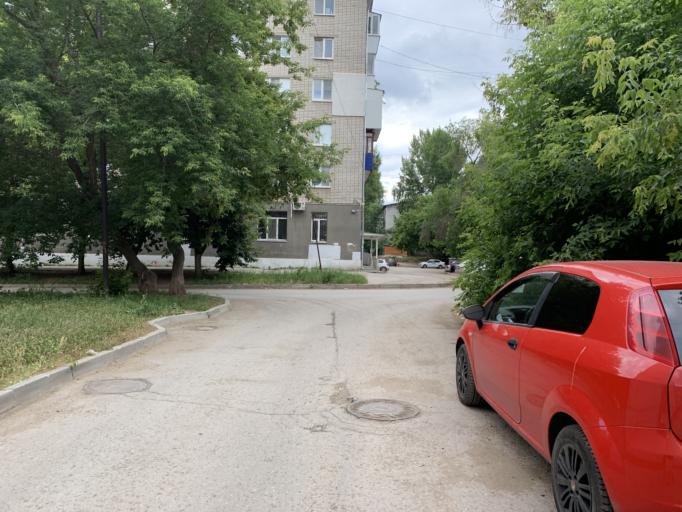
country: RU
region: Samara
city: Samara
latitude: 53.2145
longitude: 50.1707
